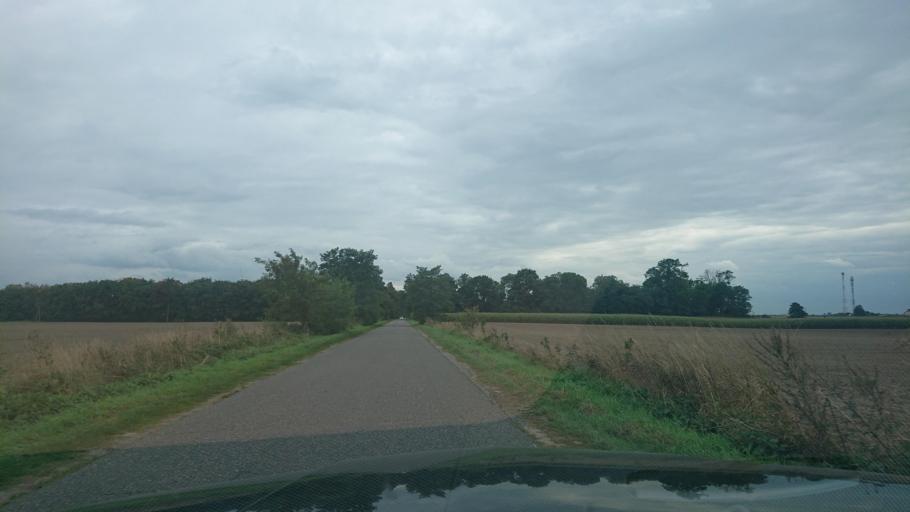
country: PL
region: Greater Poland Voivodeship
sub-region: Powiat gnieznienski
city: Niechanowo
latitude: 52.4599
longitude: 17.6200
